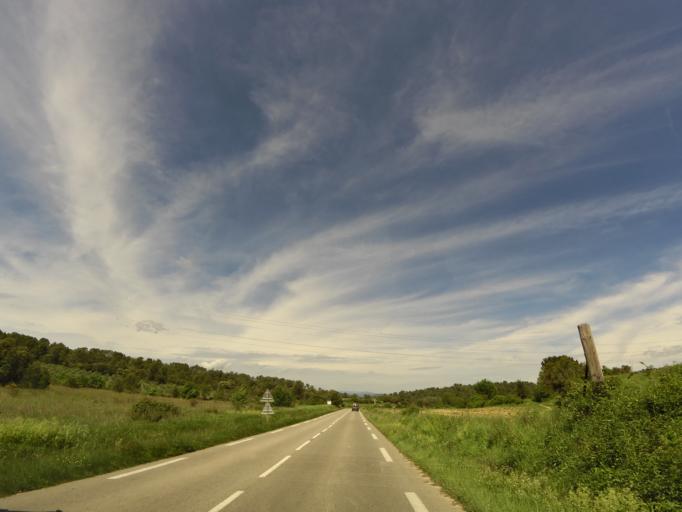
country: FR
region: Languedoc-Roussillon
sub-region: Departement du Gard
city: Sommieres
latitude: 43.8198
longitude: 4.0524
